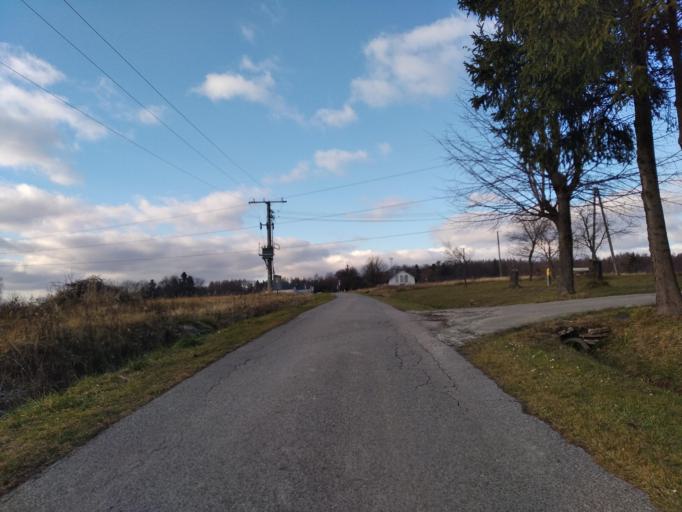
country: PL
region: Subcarpathian Voivodeship
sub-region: Powiat strzyzowski
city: Babica
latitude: 49.9451
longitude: 21.8780
